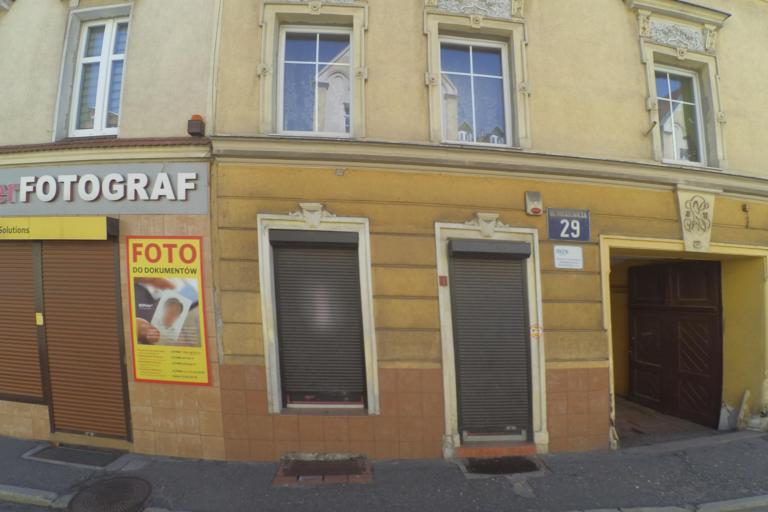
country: PL
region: Lower Silesian Voivodeship
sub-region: Powiat walbrzyski
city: Walbrzych
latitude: 50.7642
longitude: 16.2842
